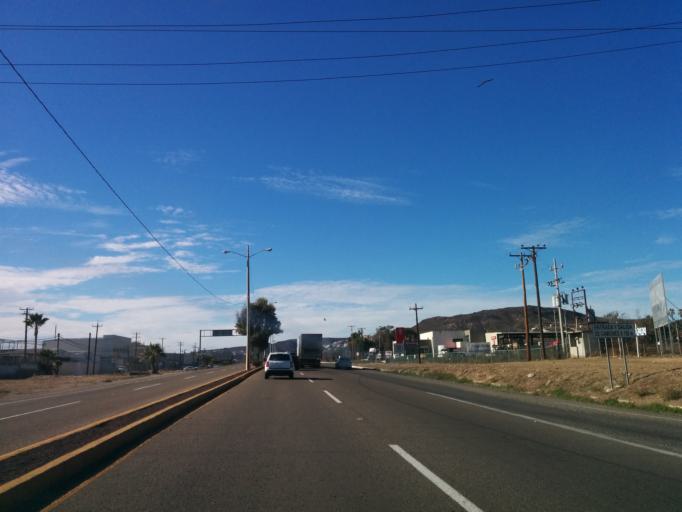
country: MX
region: Baja California
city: El Sauzal
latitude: 31.8994
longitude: -116.7061
